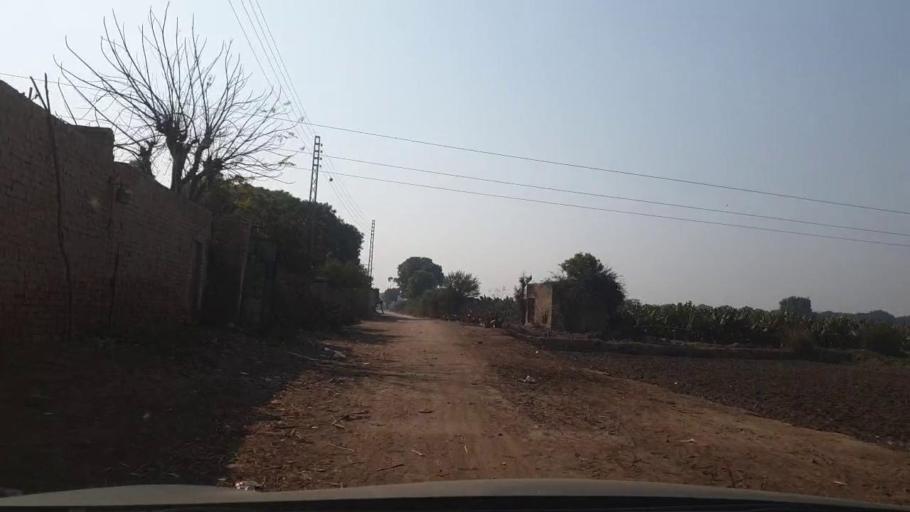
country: PK
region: Sindh
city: Tando Allahyar
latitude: 25.4857
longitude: 68.7562
